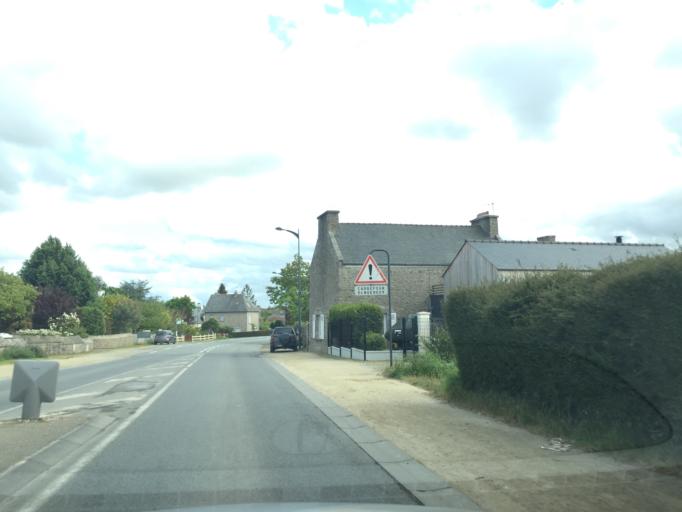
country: FR
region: Brittany
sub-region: Departement des Cotes-d'Armor
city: Lancieux
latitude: 48.5994
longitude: -2.1499
